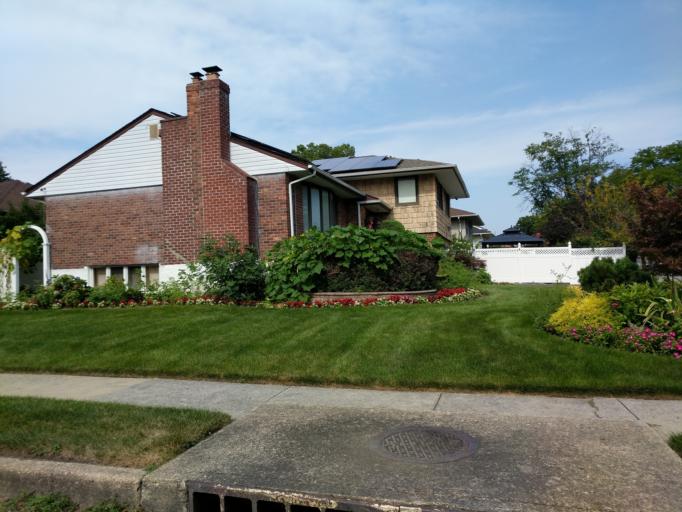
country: US
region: New York
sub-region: Nassau County
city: South Valley Stream
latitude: 40.6469
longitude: -73.7307
